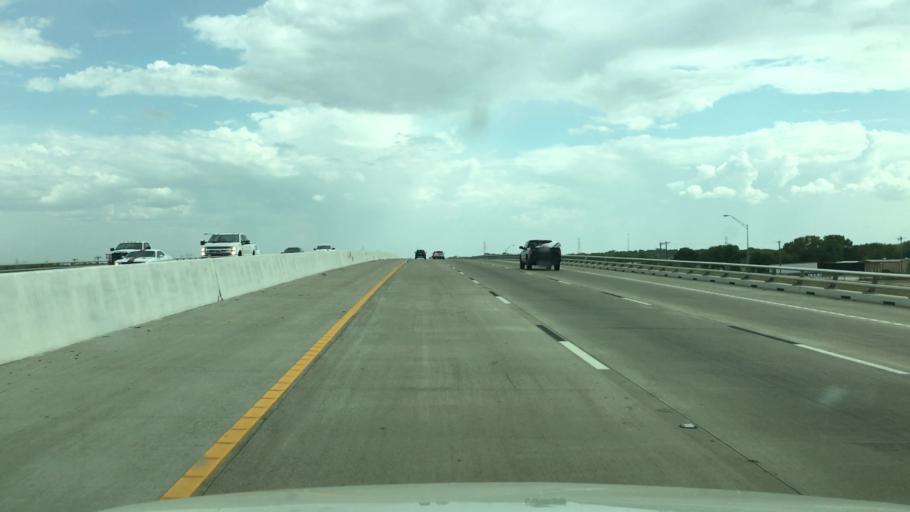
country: US
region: Texas
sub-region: McLennan County
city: Northcrest
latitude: 31.7175
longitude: -97.1026
